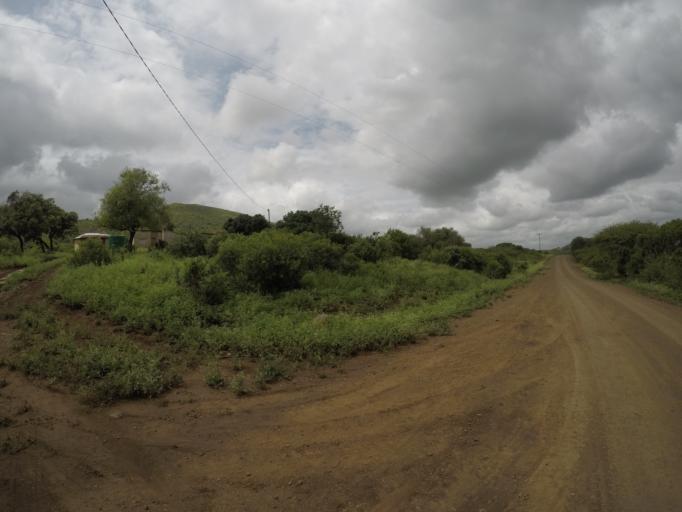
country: ZA
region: KwaZulu-Natal
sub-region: uThungulu District Municipality
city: Empangeni
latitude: -28.5740
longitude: 31.8718
